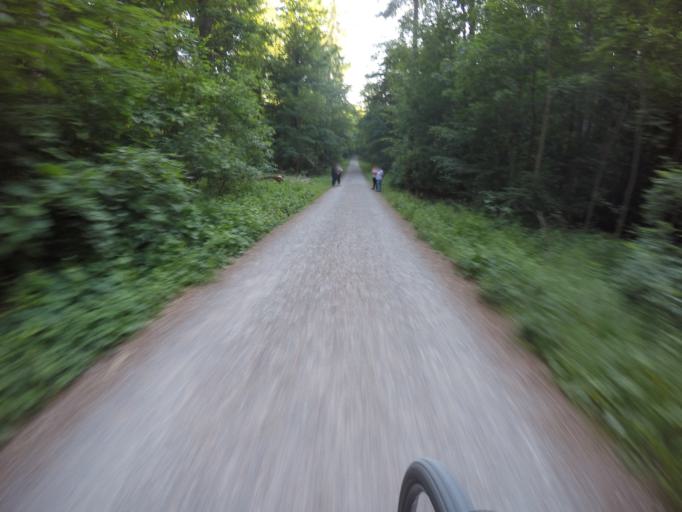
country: DE
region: Baden-Wuerttemberg
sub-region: Regierungsbezirk Stuttgart
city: Fellbach
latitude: 48.7881
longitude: 9.2936
